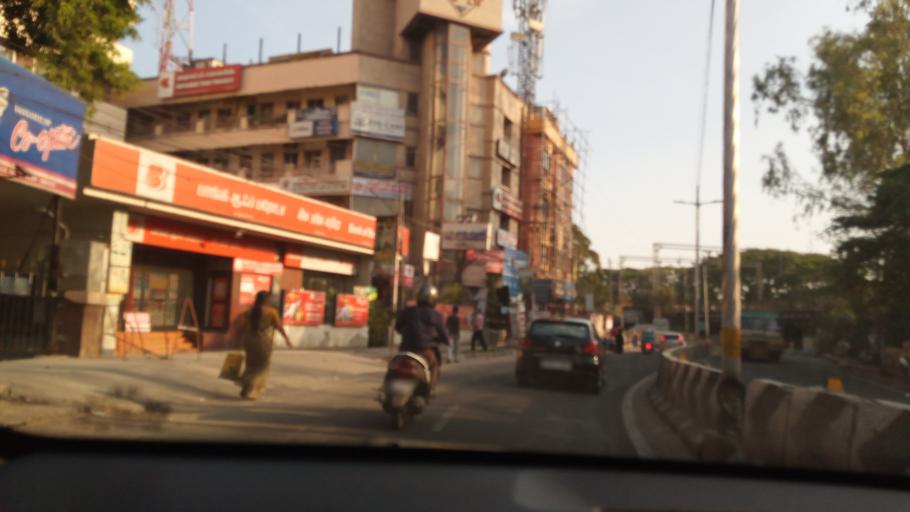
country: IN
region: Tamil Nadu
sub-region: Coimbatore
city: Coimbatore
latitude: 10.9955
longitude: 76.9684
